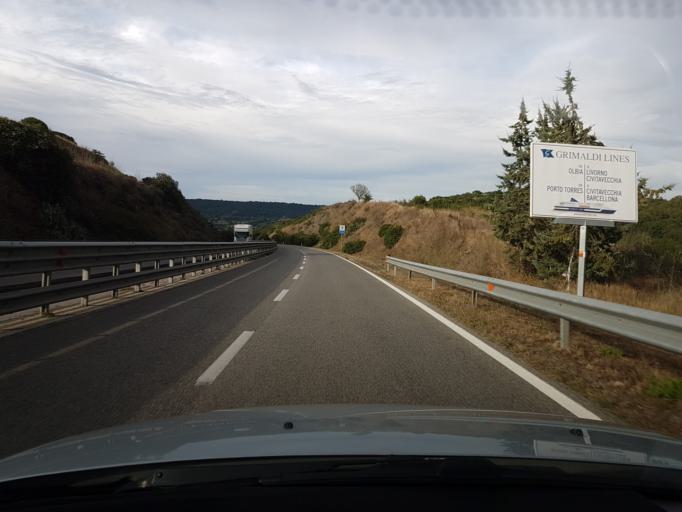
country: IT
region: Sardinia
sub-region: Provincia di Oristano
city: Soddi
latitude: 40.1343
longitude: 8.8671
